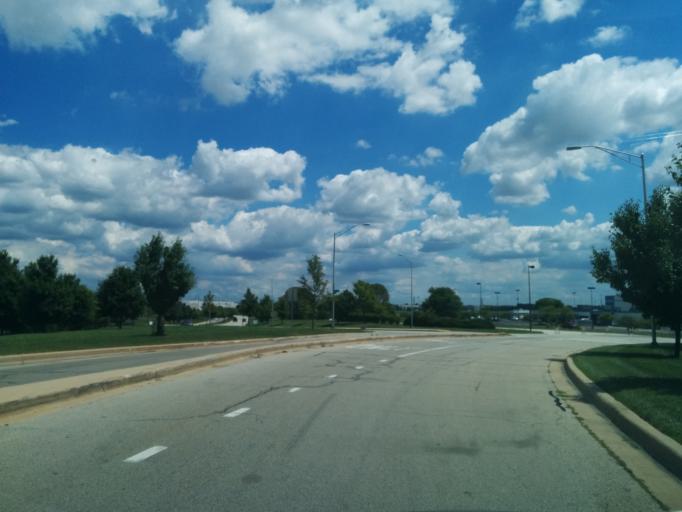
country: US
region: Illinois
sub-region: Will County
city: Romeoville
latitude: 41.6754
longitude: -88.1178
